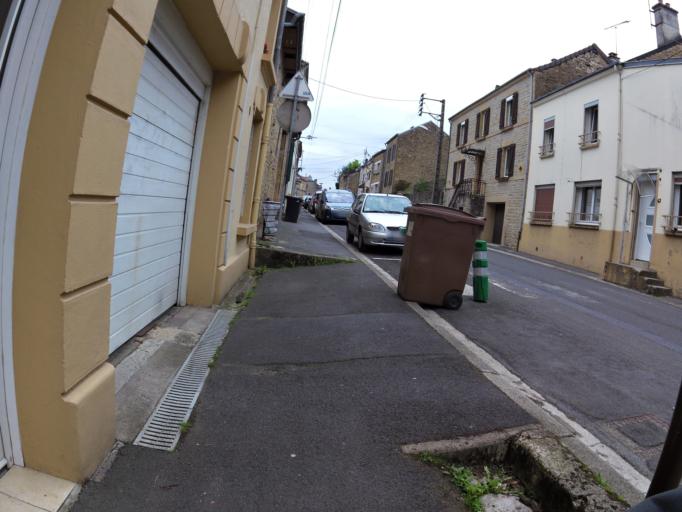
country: FR
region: Champagne-Ardenne
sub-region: Departement des Ardennes
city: Montcy-Notre-Dame
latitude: 49.7585
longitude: 4.7389
